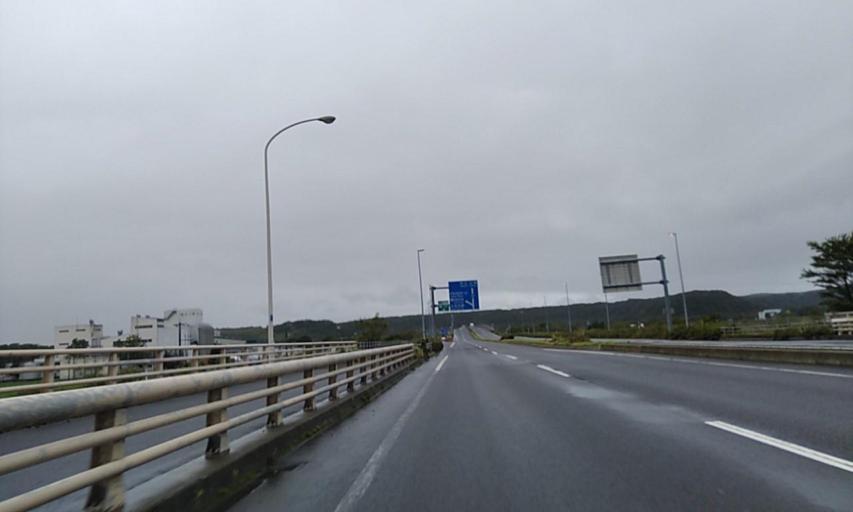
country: JP
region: Hokkaido
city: Kushiro
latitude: 43.0216
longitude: 144.2692
